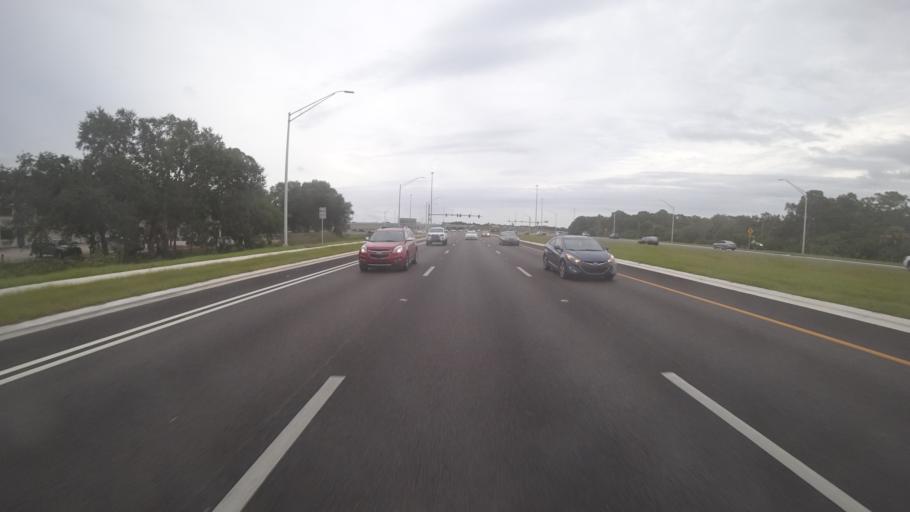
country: US
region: Florida
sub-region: Manatee County
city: Ellenton
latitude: 27.4924
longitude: -82.4772
